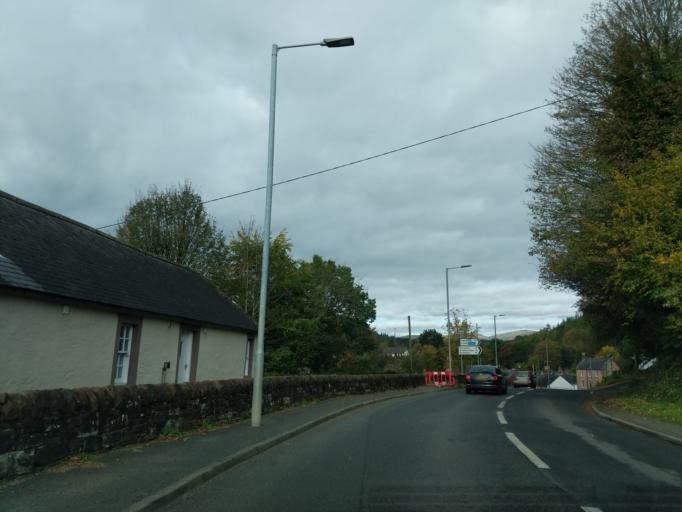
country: GB
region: Scotland
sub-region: Dumfries and Galloway
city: Thornhill
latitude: 55.2623
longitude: -3.7803
